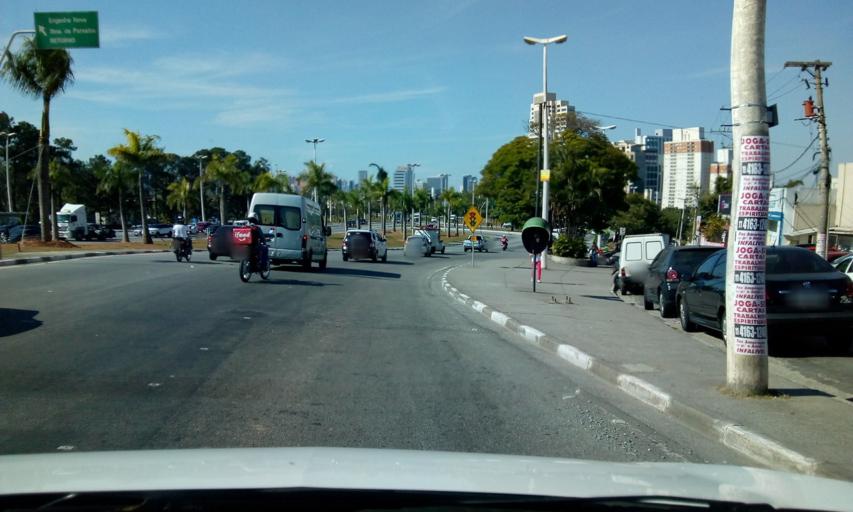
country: BR
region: Sao Paulo
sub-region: Barueri
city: Barueri
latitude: -23.5061
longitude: -46.8755
